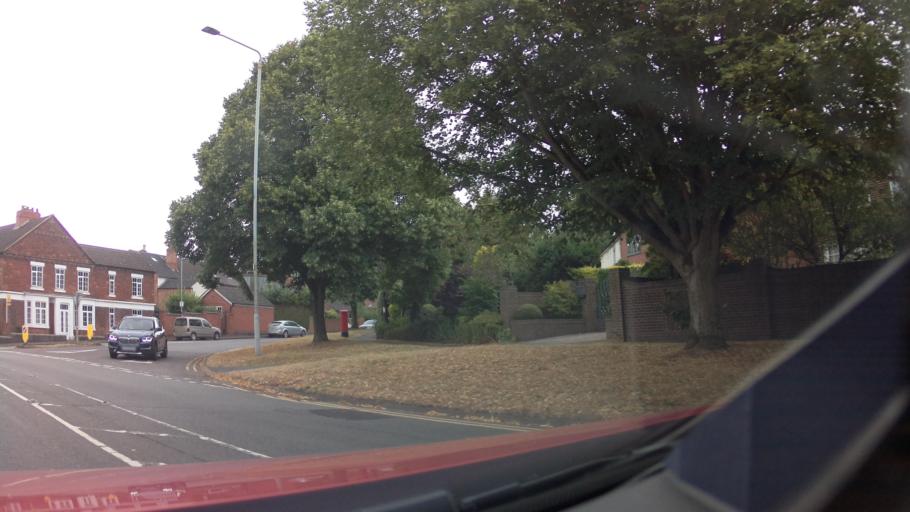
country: GB
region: England
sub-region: Leicestershire
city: Ashby de la Zouch
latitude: 52.7481
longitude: -1.4791
